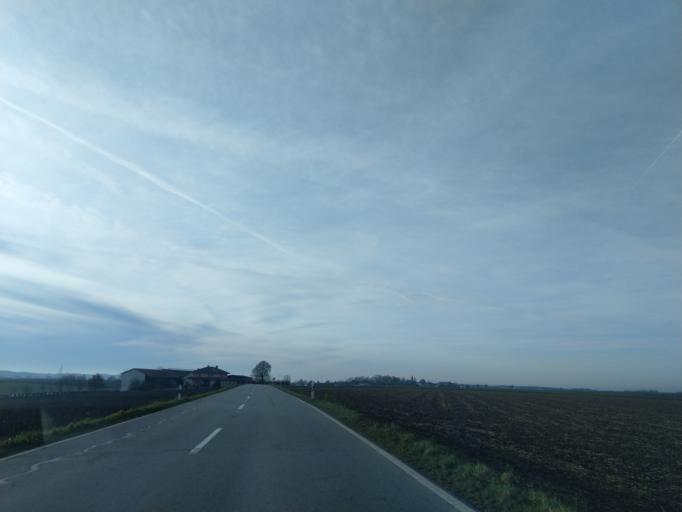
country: DE
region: Bavaria
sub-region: Lower Bavaria
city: Osterhofen
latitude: 48.7007
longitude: 12.9914
